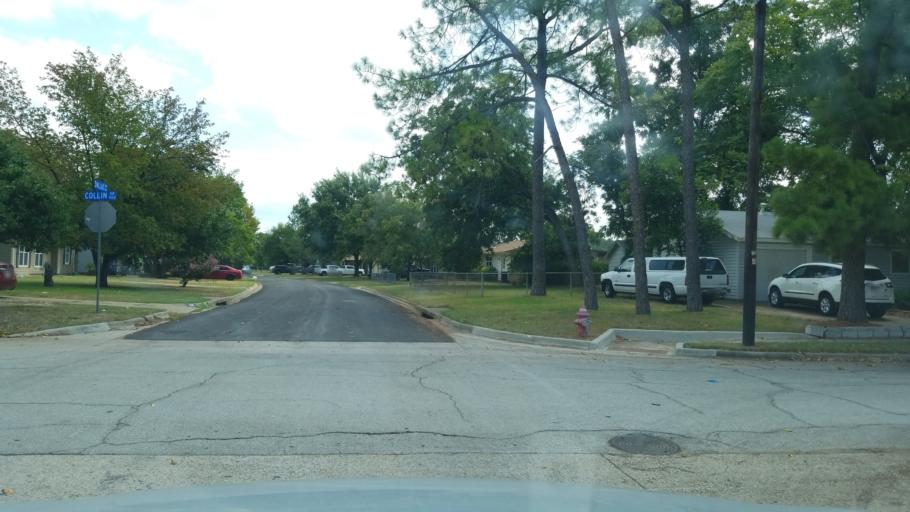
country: US
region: Texas
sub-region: Tarrant County
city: Euless
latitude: 32.8488
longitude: -97.0857
